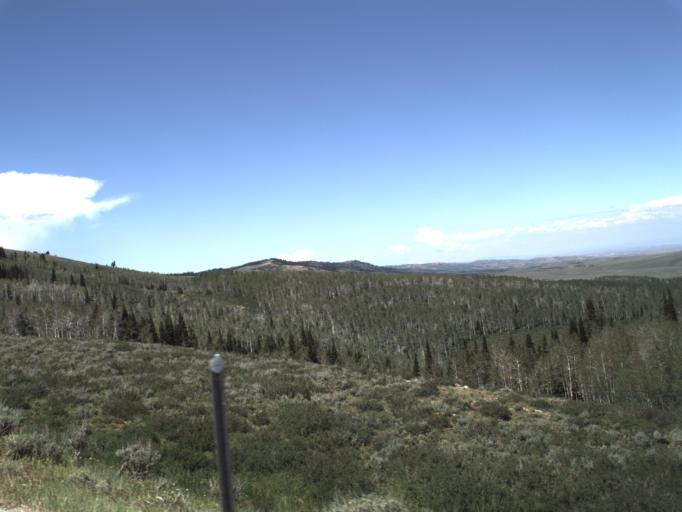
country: US
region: Utah
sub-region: Rich County
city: Randolph
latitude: 41.4738
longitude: -111.4534
